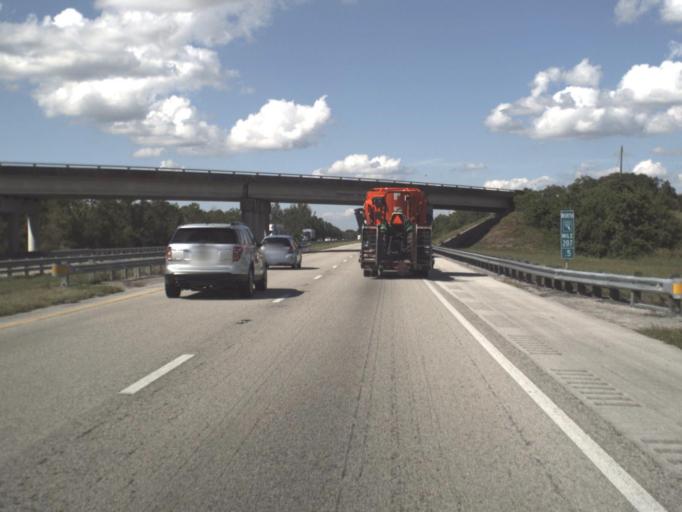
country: US
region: Florida
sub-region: Brevard County
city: June Park
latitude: 27.8655
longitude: -81.0136
